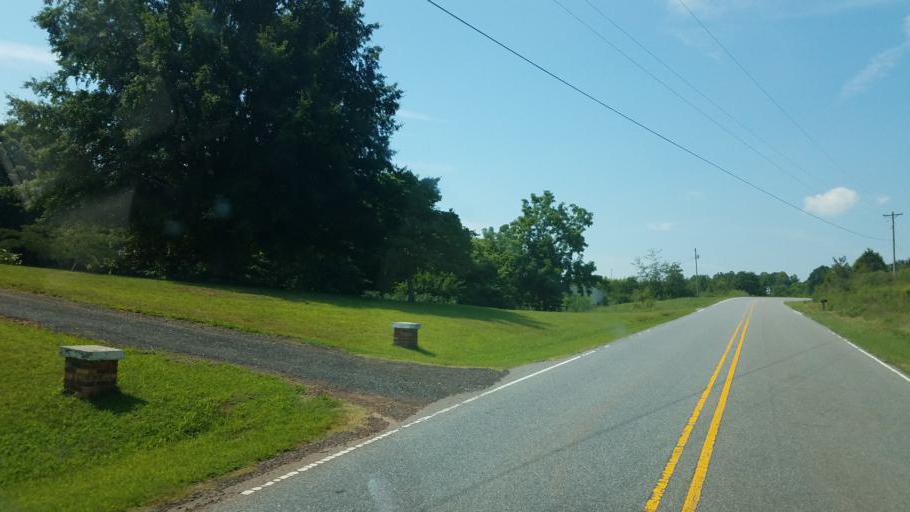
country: US
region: North Carolina
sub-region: Burke County
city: Icard
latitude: 35.5692
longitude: -81.5092
